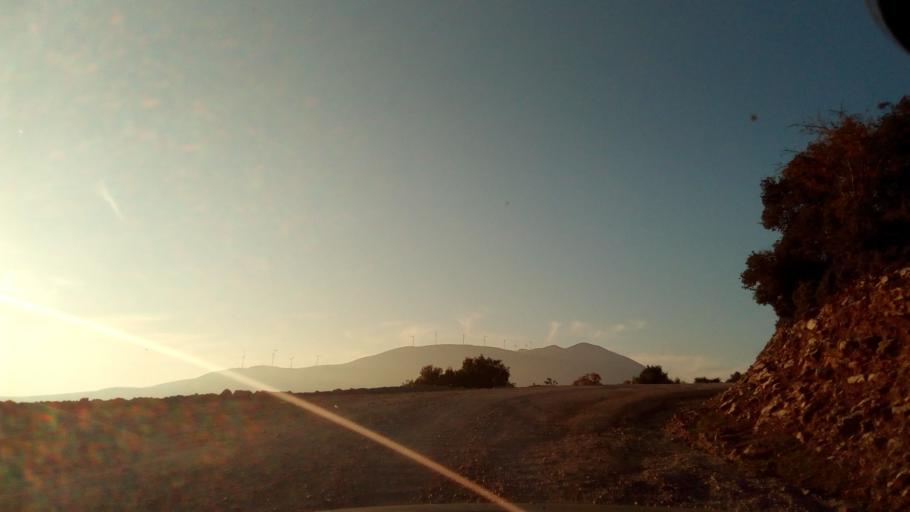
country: GR
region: West Greece
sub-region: Nomos Aitolias kai Akarnanias
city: Nafpaktos
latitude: 38.4378
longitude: 21.8489
